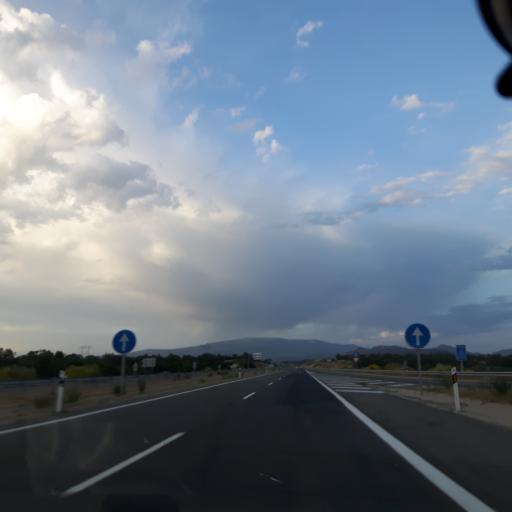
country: ES
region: Castille and Leon
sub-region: Provincia de Salamanca
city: Fuentes de Bejar
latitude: 40.5223
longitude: -5.6721
